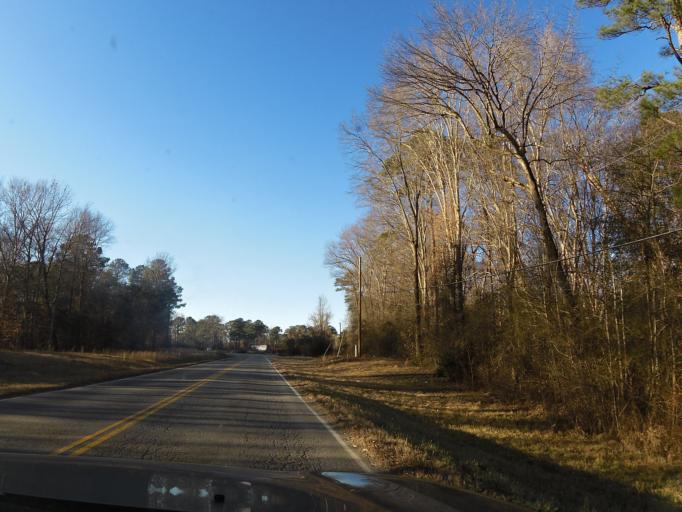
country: US
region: Virginia
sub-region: City of Franklin
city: Franklin
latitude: 36.6766
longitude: -76.9018
